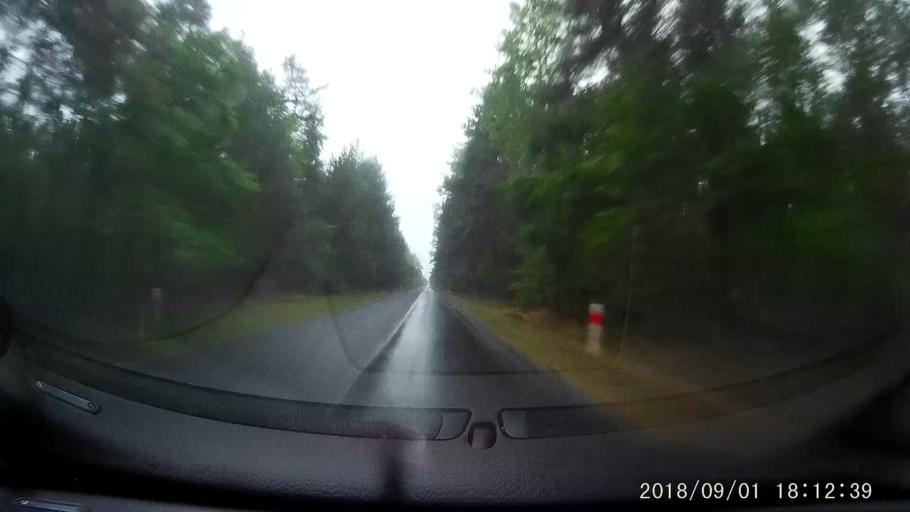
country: PL
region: Lower Silesian Voivodeship
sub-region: Powiat zgorzelecki
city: Piensk
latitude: 51.3111
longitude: 15.0688
